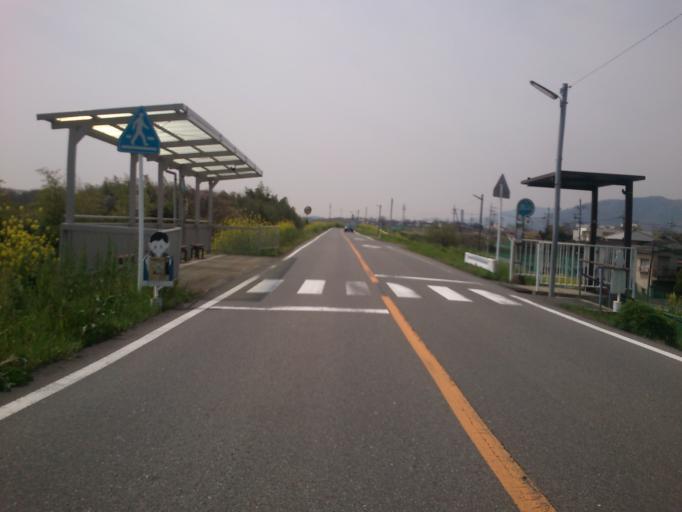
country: JP
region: Kyoto
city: Yawata
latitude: 34.9169
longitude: 135.7209
